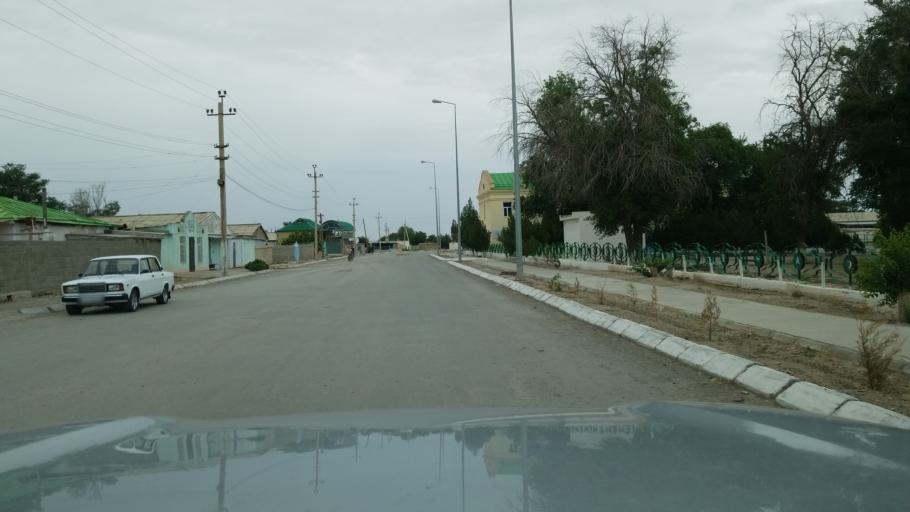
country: TM
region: Balkan
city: Serdar
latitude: 38.9848
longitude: 56.2755
